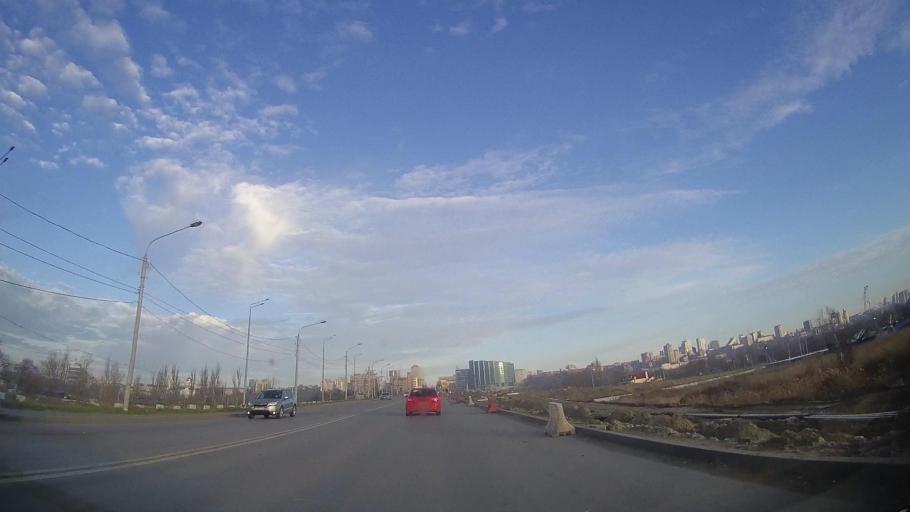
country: RU
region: Rostov
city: Rostov-na-Donu
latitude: 47.2086
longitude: 39.7250
